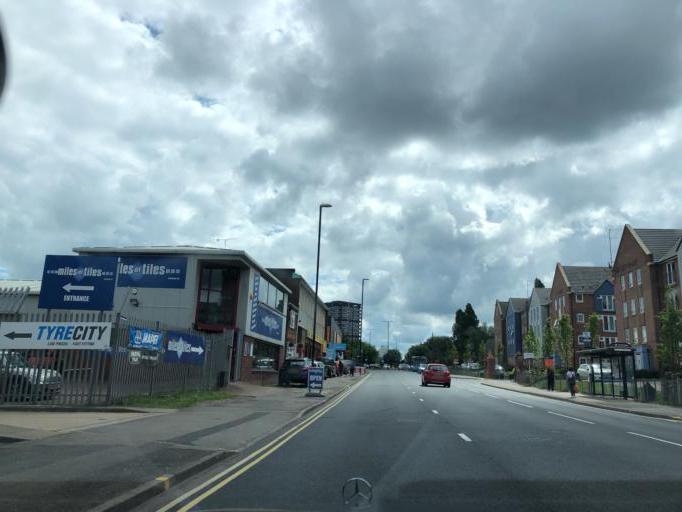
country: GB
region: England
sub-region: Coventry
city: Coventry
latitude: 52.4172
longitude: -1.5084
